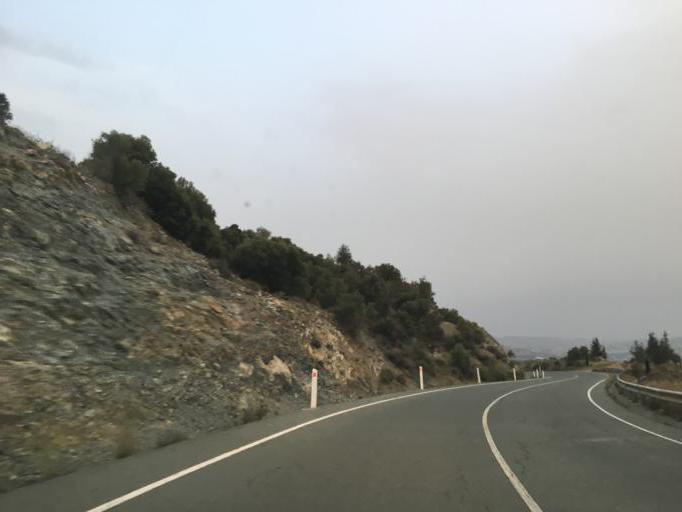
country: CY
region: Limassol
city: Parekklisha
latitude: 34.7972
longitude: 33.1517
